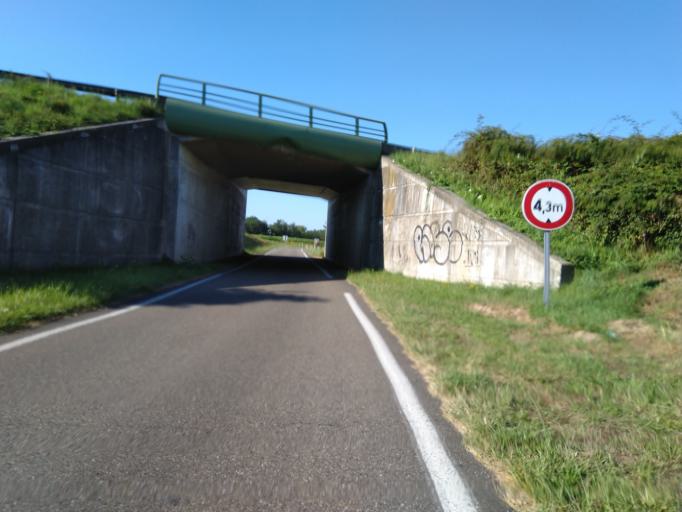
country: FR
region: Aquitaine
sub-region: Departement des Landes
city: Saint-Vincent-de-Paul
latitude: 43.7374
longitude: -1.0261
